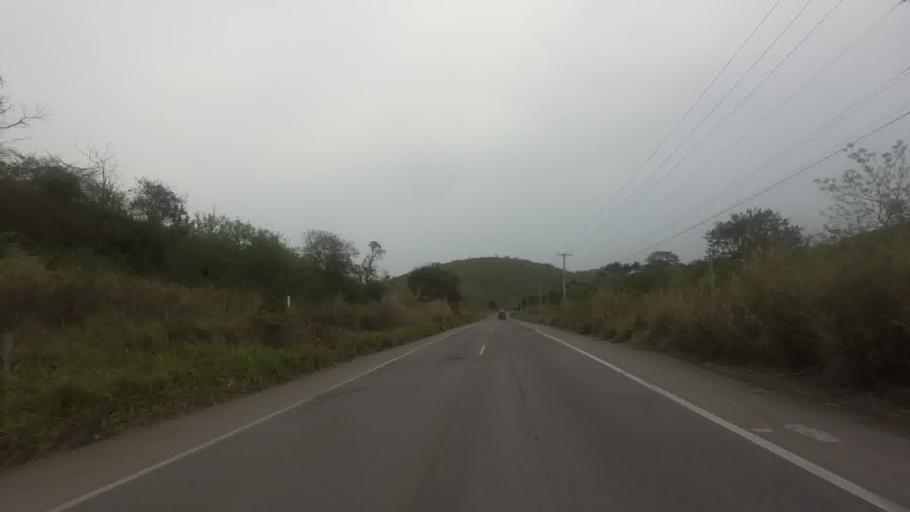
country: BR
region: Rio de Janeiro
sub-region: Santo Antonio De Padua
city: Santo Antonio de Padua
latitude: -21.6030
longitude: -42.2394
